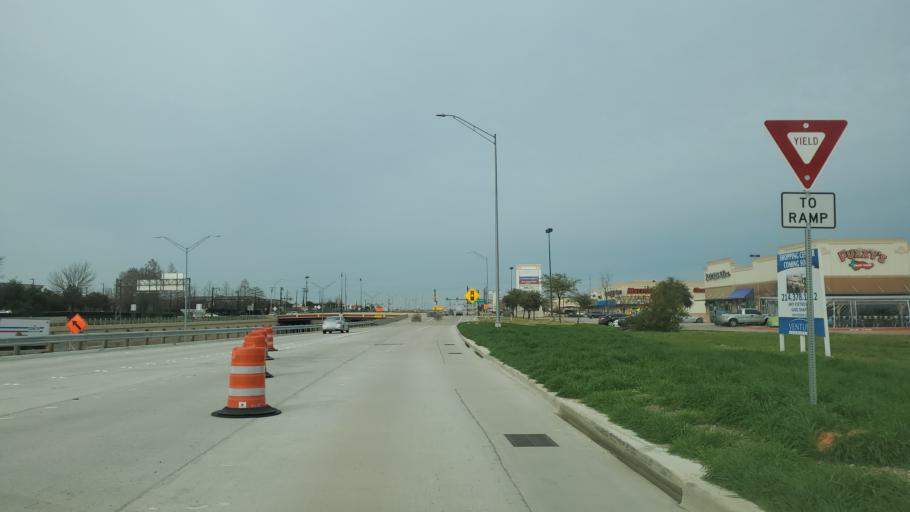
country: US
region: Texas
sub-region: Dallas County
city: Coppell
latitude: 32.9679
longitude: -97.0366
